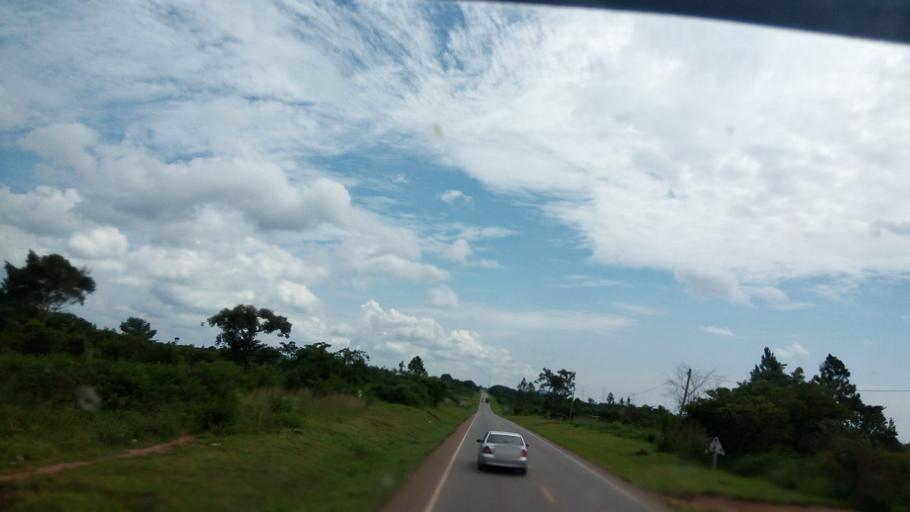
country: UG
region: Central Region
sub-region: Nakasongola District
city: Nakasongola
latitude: 1.2263
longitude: 32.4647
